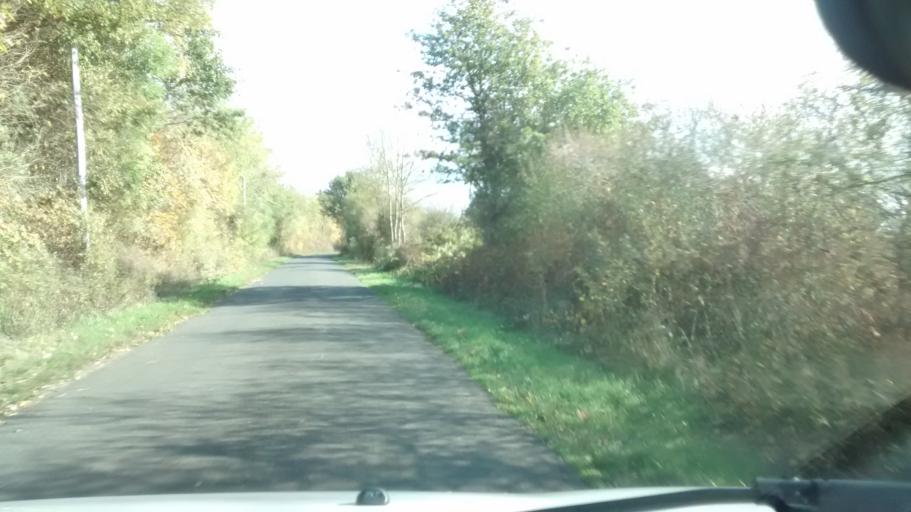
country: FR
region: Pays de la Loire
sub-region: Departement de Maine-et-Loire
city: Feneu
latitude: 47.5624
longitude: -0.5816
